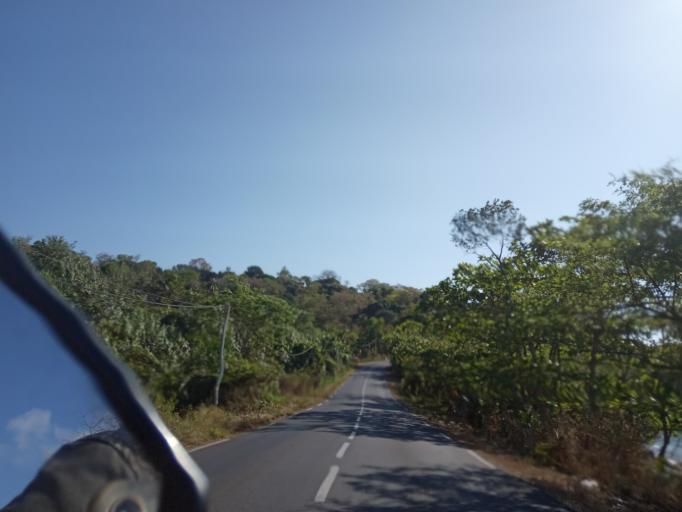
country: YT
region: Bandrele
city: Bandrele
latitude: -12.9260
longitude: 45.1793
